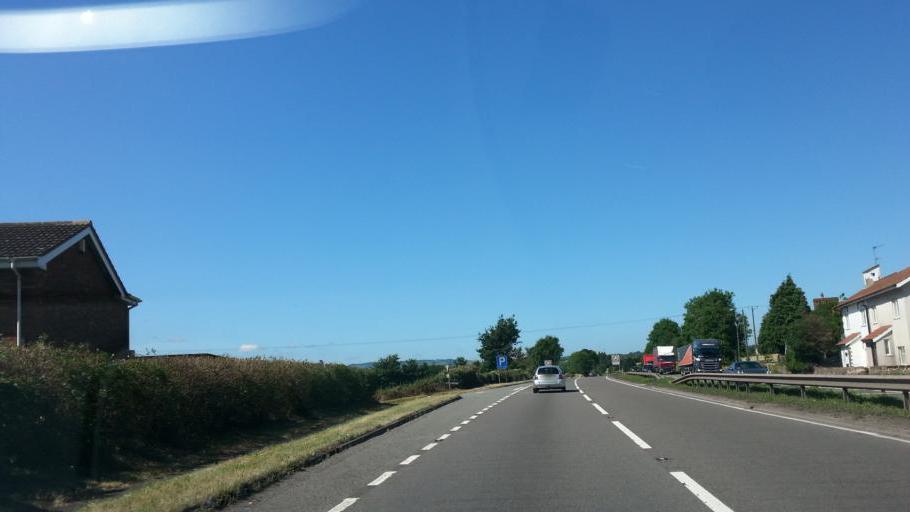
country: GB
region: England
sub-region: Herefordshire
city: Walford
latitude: 51.9150
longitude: -2.6038
